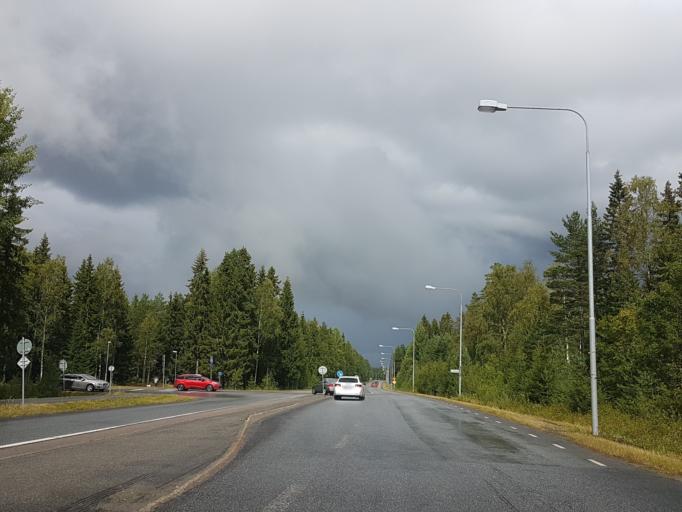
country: SE
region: Vaesterbotten
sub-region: Umea Kommun
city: Ersmark
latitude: 63.8521
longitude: 20.3438
